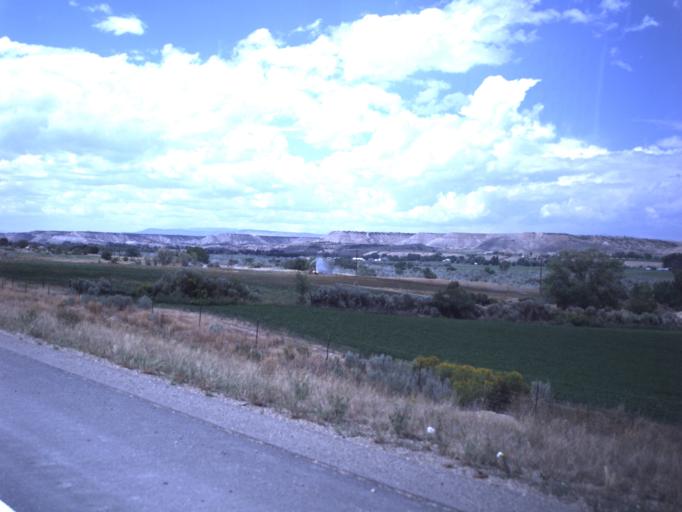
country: US
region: Utah
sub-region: Duchesne County
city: Duchesne
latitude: 40.1695
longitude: -110.3073
